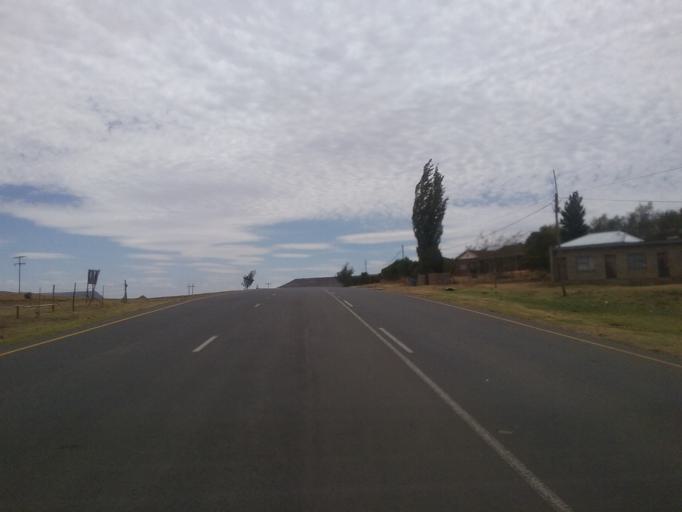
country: LS
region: Maseru
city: Nako
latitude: -29.6330
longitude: 27.4811
